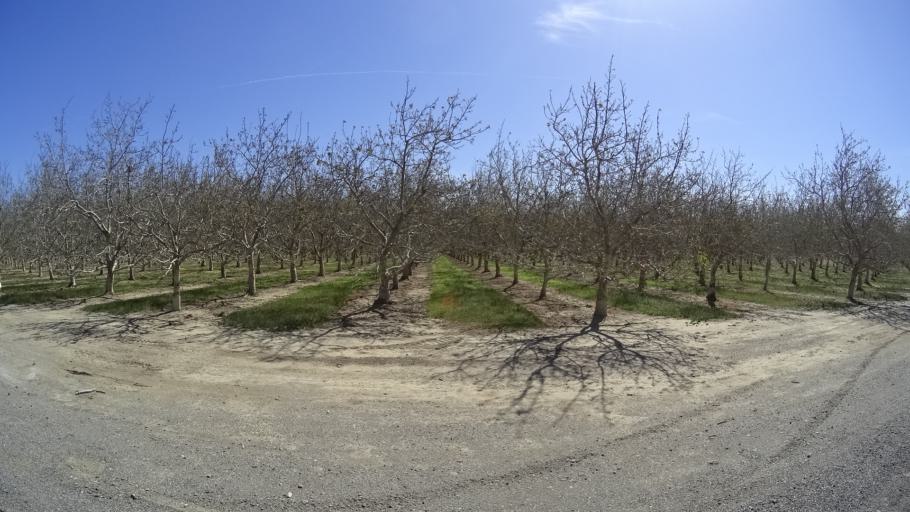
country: US
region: California
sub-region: Glenn County
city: Hamilton City
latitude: 39.6499
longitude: -122.1037
